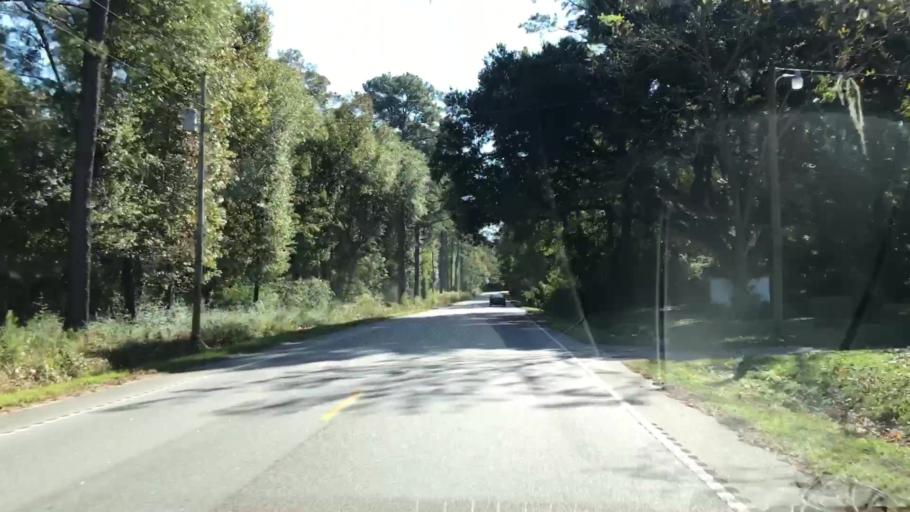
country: US
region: South Carolina
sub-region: Jasper County
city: Ridgeland
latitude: 32.5717
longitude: -80.9217
